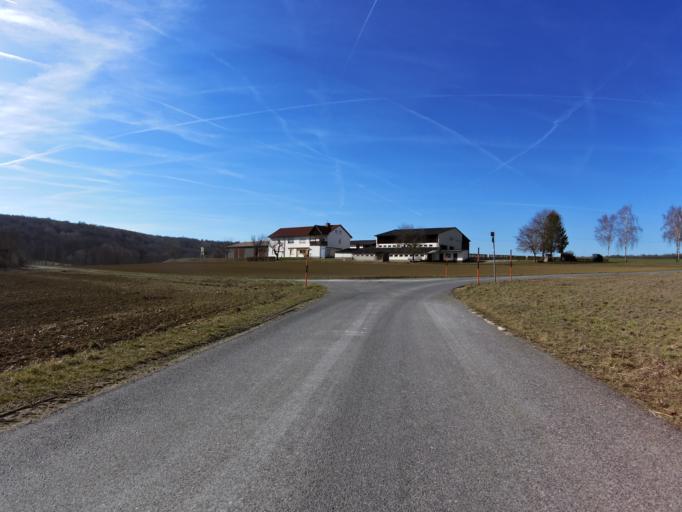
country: DE
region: Bavaria
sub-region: Regierungsbezirk Unterfranken
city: Kurnach
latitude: 49.8574
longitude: 10.0086
